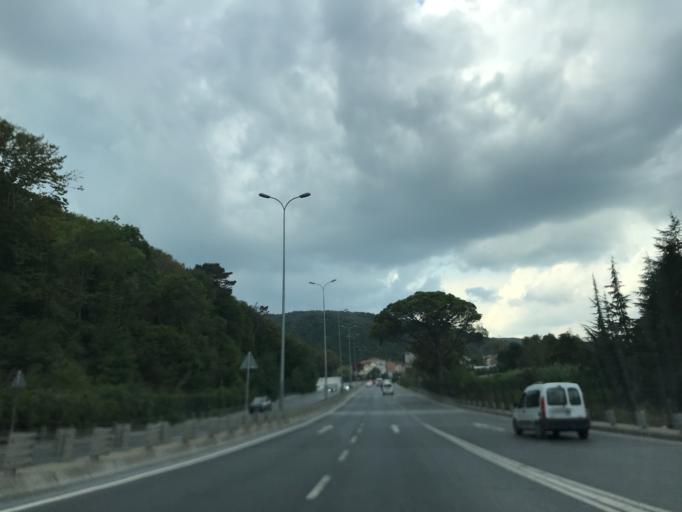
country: TR
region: Istanbul
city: Arikoey
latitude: 41.1528
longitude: 29.0294
